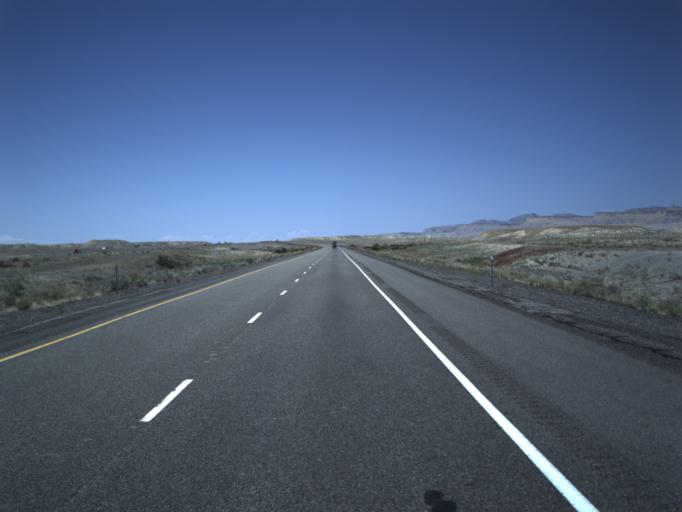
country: US
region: Utah
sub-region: Grand County
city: Moab
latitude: 38.9416
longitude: -109.5174
